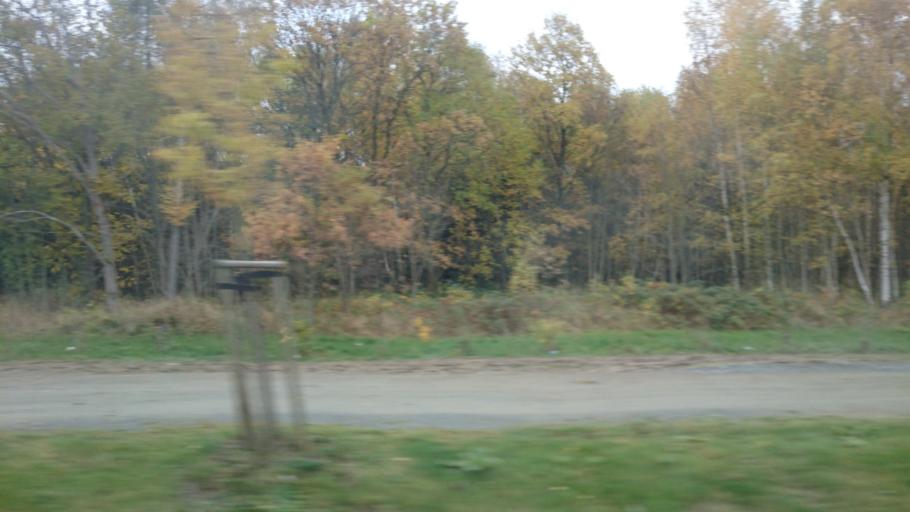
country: DE
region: Thuringia
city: Dittersdorf
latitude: 50.6523
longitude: 11.8163
